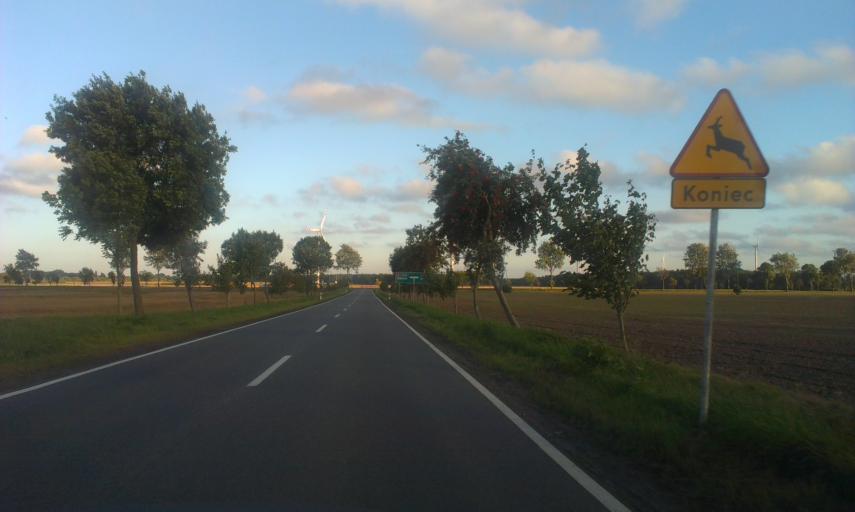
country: PL
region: West Pomeranian Voivodeship
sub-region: Powiat slawienski
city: Slawno
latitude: 54.3283
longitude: 16.5548
